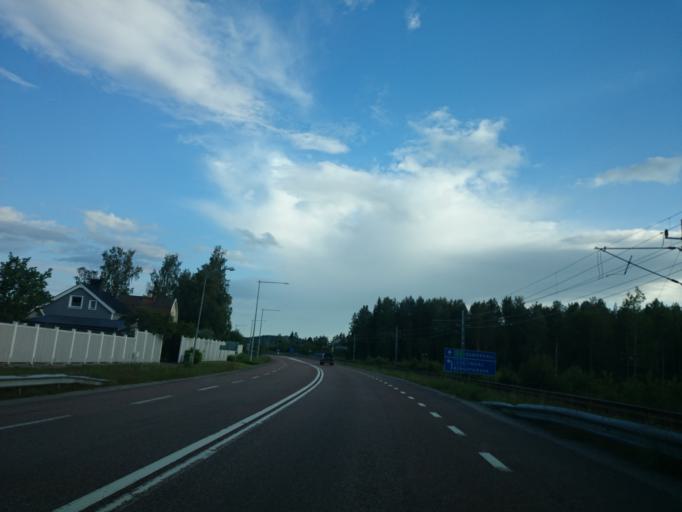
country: SE
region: Vaesternorrland
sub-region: Timra Kommun
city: Bergeforsen
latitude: 62.5300
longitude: 17.3861
